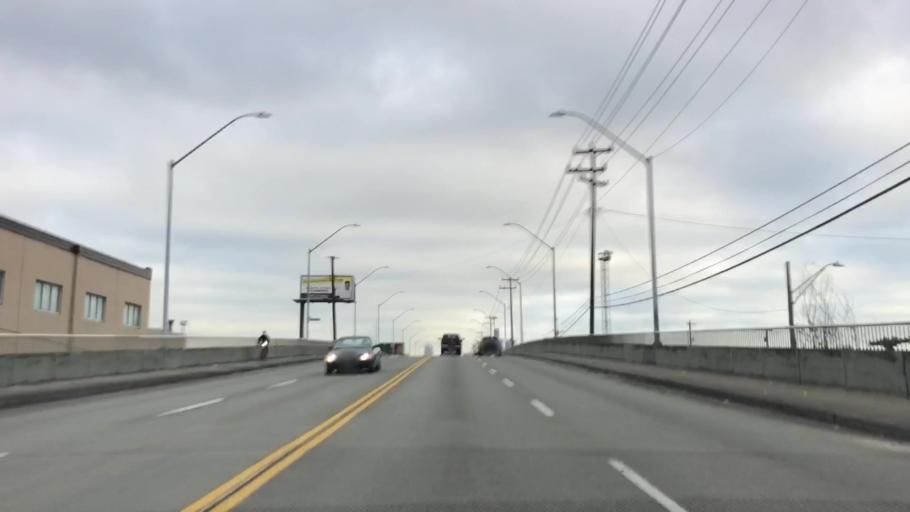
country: US
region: Washington
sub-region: King County
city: Seattle
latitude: 47.5607
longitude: -122.3342
